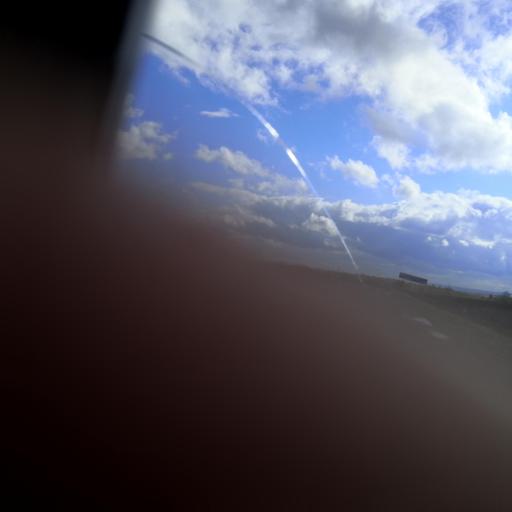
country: RU
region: Bashkortostan
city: Pavlovka
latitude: 55.3229
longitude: 56.3512
